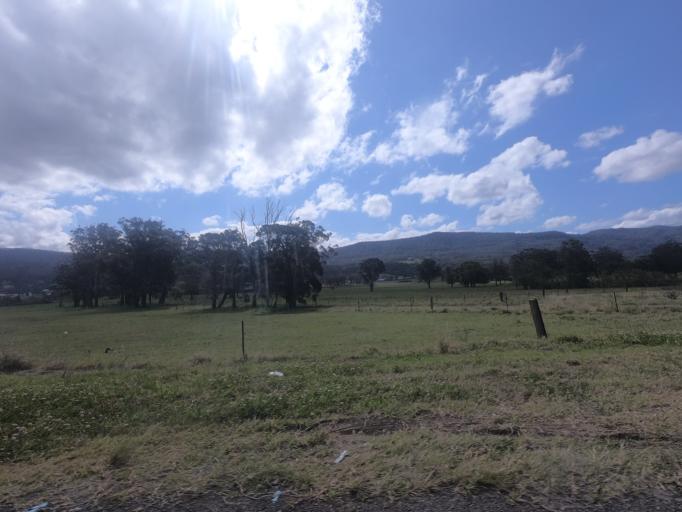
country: AU
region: New South Wales
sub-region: Wollongong
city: Dapto
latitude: -34.4781
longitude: 150.7840
